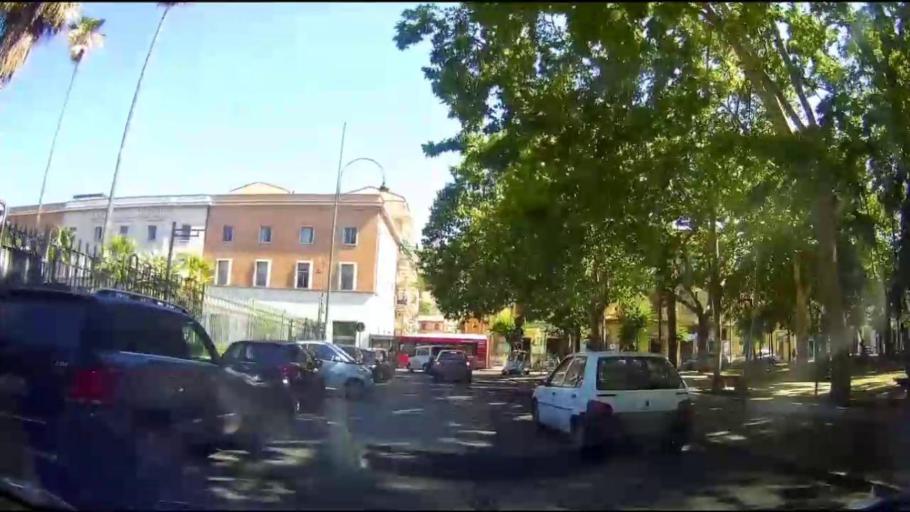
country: IT
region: Calabria
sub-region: Provincia di Cosenza
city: Cosenza
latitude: 39.2943
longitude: 16.2543
